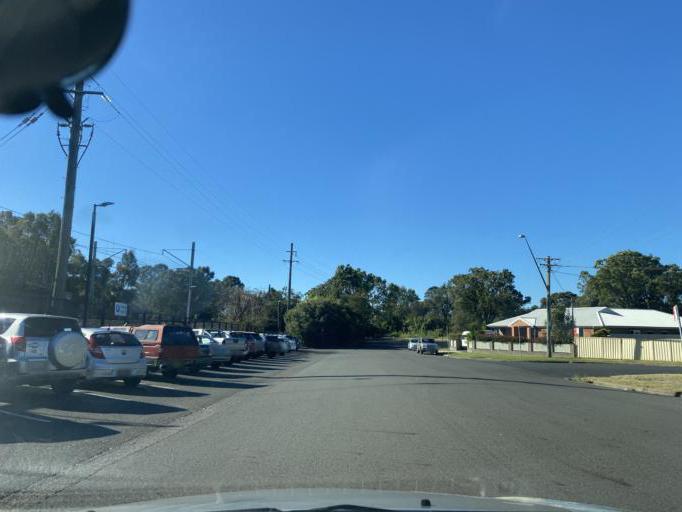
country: AU
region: New South Wales
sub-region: Campbelltown Municipality
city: Ingleburn
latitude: -33.9846
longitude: 150.8795
